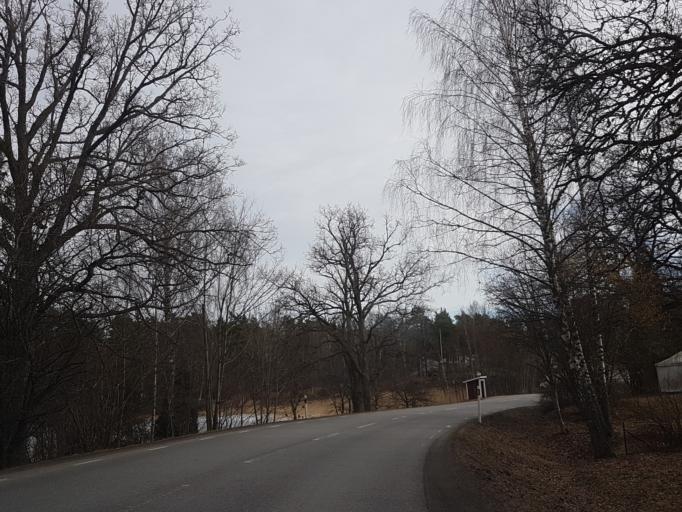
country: SE
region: Stockholm
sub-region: Norrtalje Kommun
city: Norrtalje
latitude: 59.6779
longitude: 18.7636
